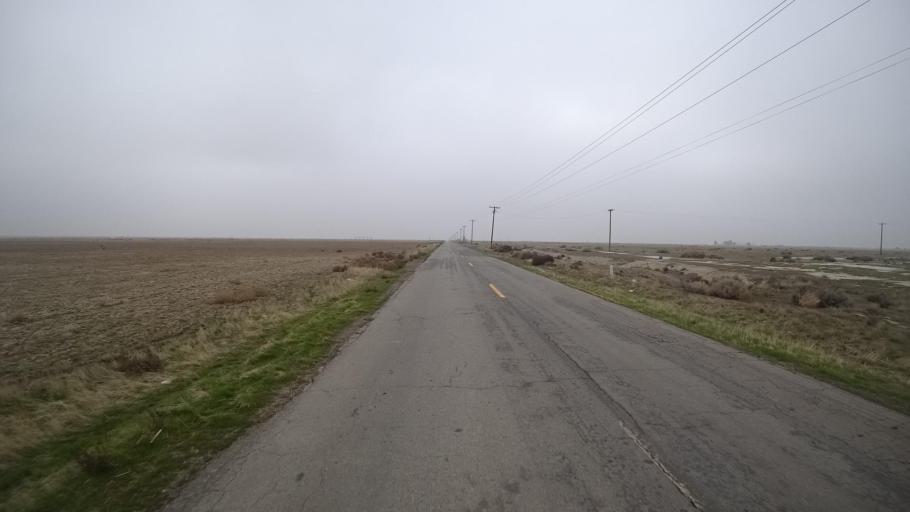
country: US
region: California
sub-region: Tulare County
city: Alpaugh
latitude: 35.7174
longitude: -119.4661
